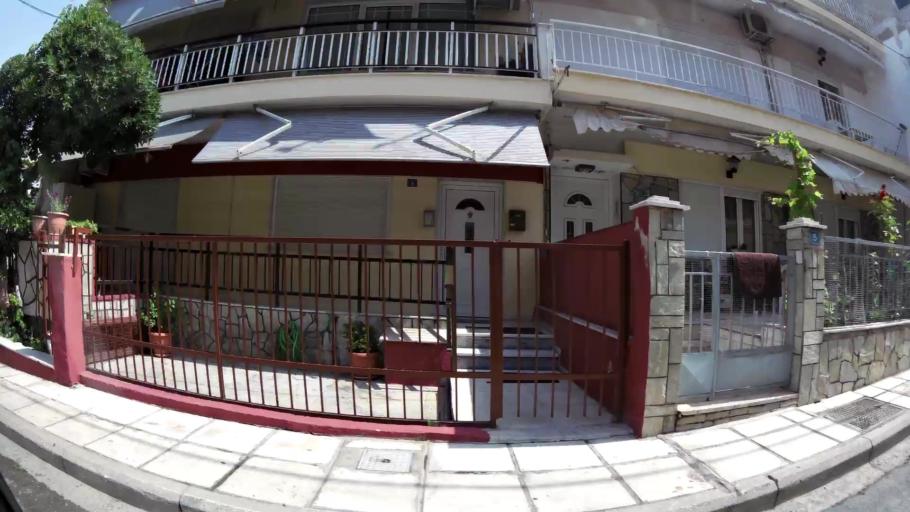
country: GR
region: Central Macedonia
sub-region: Nomos Thessalonikis
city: Stavroupoli
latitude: 40.6737
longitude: 22.9352
